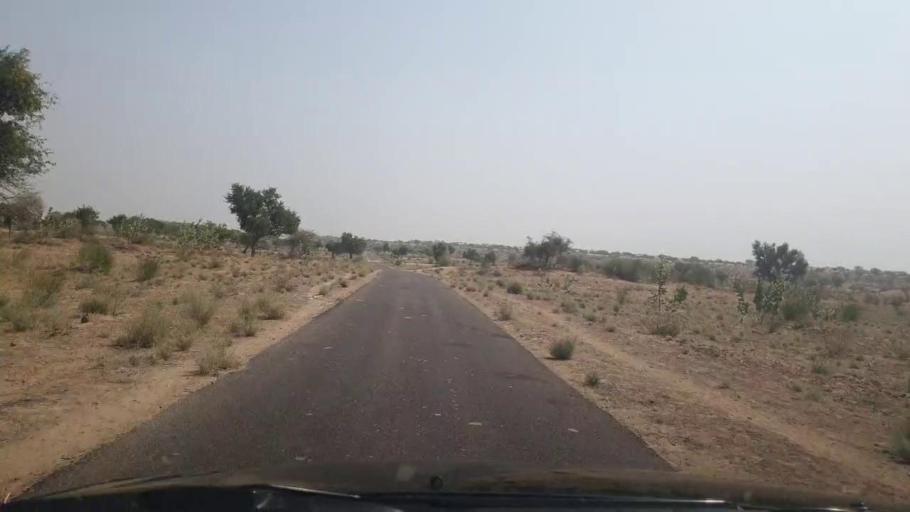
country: PK
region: Sindh
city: Islamkot
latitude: 24.9449
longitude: 70.4047
